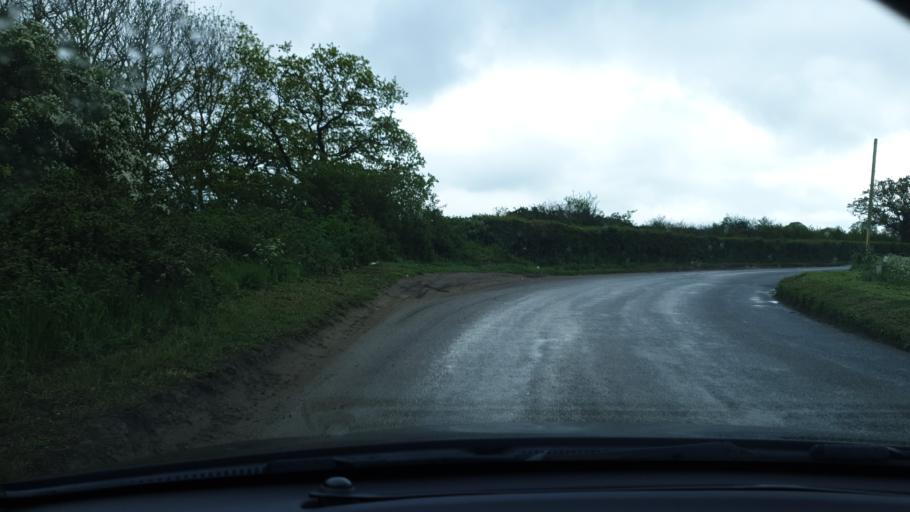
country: GB
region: England
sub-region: Essex
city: Wivenhoe
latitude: 51.9117
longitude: 0.9782
